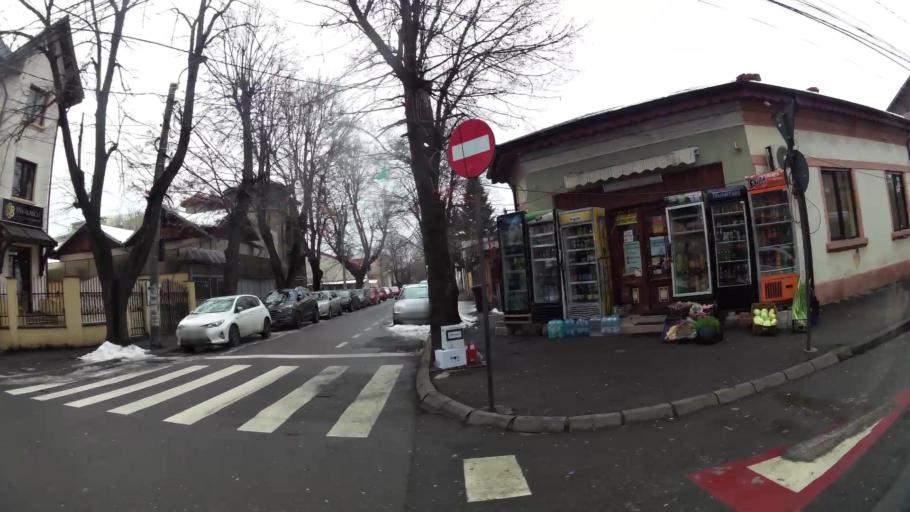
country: RO
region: Bucuresti
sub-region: Municipiul Bucuresti
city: Bucuresti
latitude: 44.4619
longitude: 26.0664
